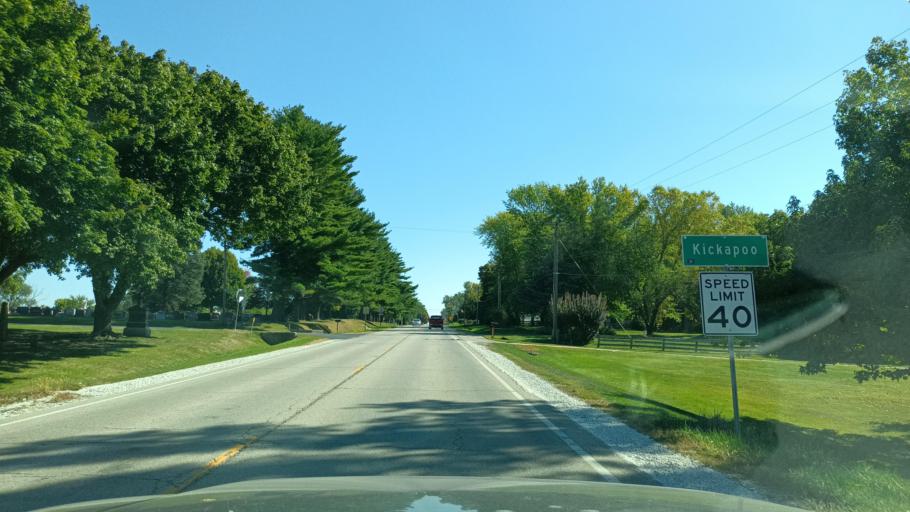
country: US
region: Illinois
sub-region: Peoria County
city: Hanna City
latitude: 40.7899
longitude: -89.7569
